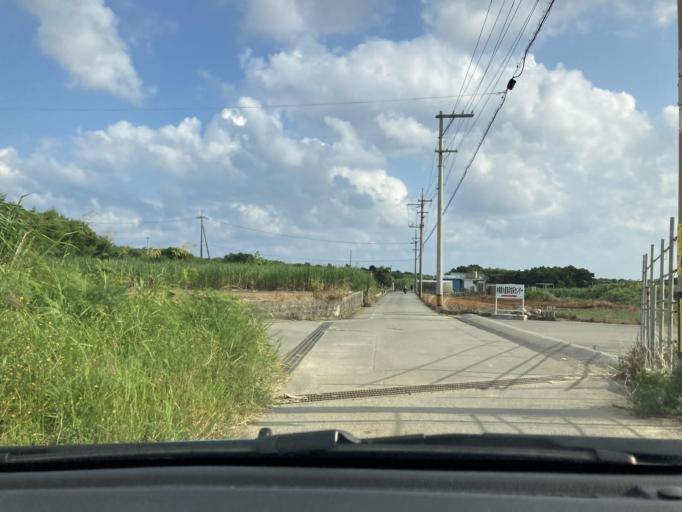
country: JP
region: Okinawa
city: Itoman
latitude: 26.0865
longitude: 127.6624
